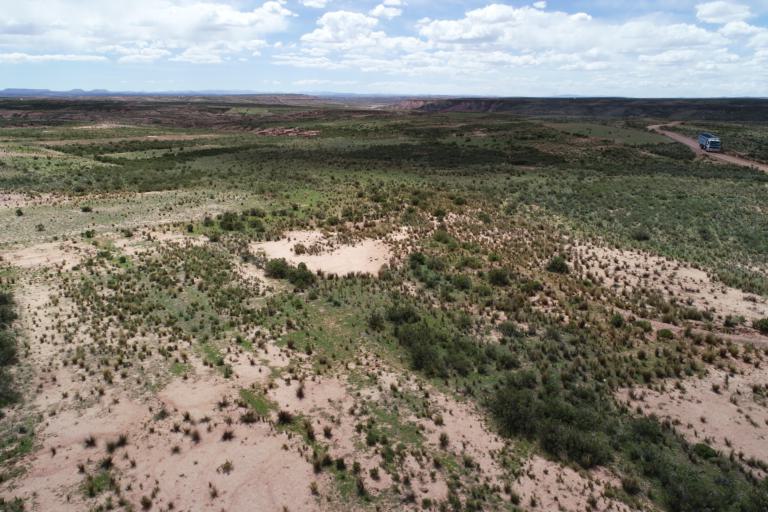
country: BO
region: La Paz
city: Curahuara de Carangas
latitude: -17.3234
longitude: -68.4999
